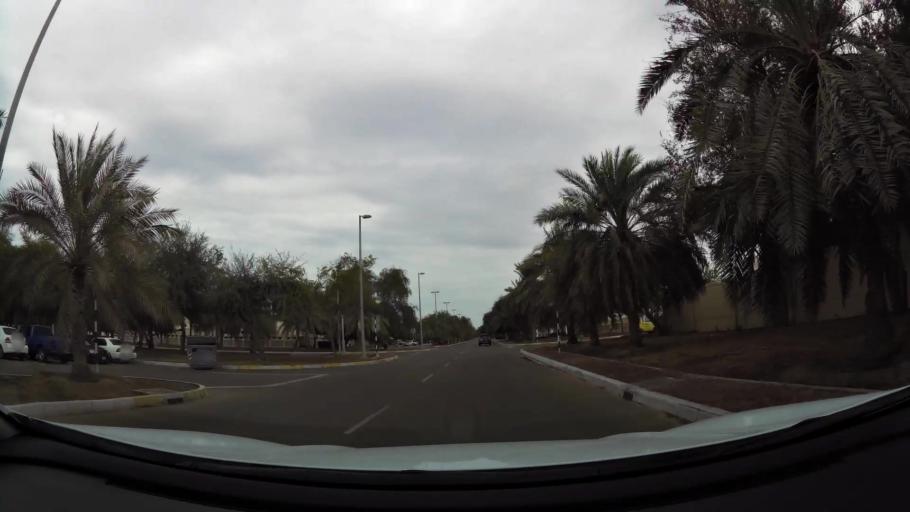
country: AE
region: Abu Dhabi
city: Abu Dhabi
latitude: 24.4260
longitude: 54.4195
